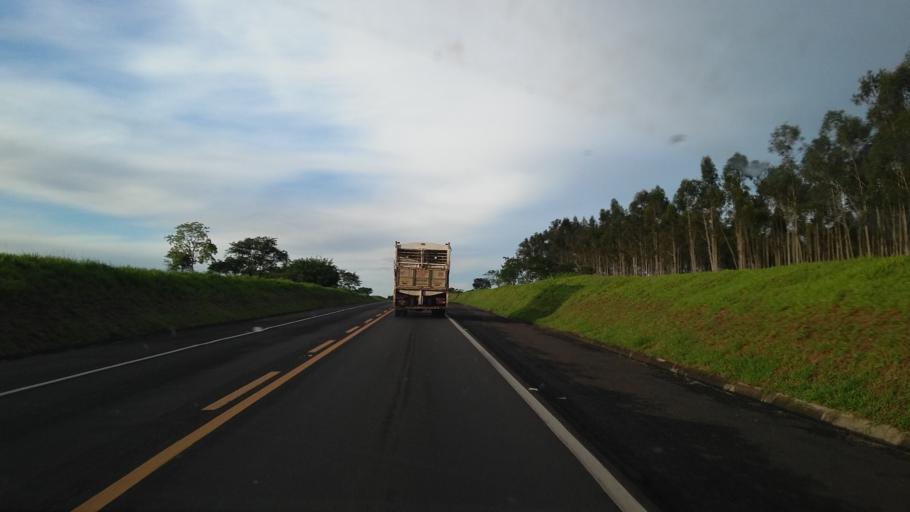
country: BR
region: Sao Paulo
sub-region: Marilia
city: Marilia
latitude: -21.9300
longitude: -49.9183
